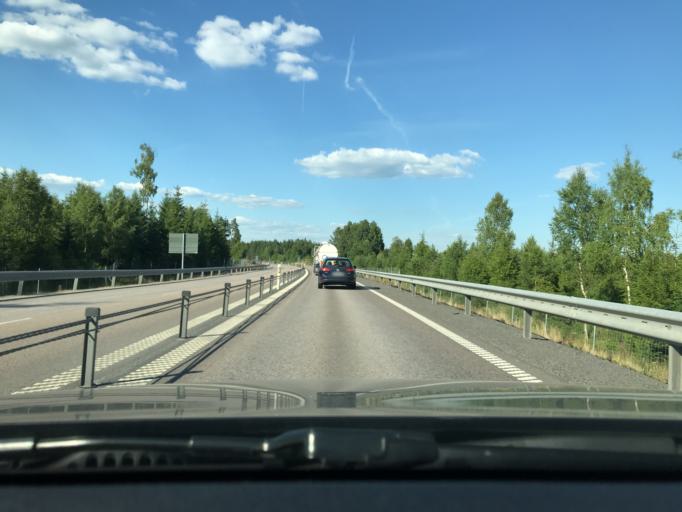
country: SE
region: Kronoberg
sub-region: Almhults Kommun
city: AElmhult
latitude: 56.6488
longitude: 14.2806
